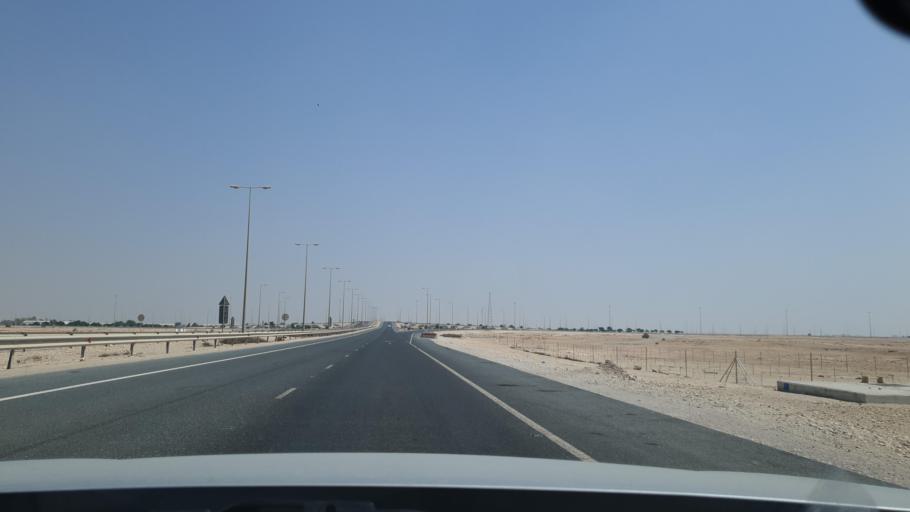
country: QA
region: Baladiyat az Za`ayin
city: Az Za`ayin
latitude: 25.6202
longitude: 51.3940
